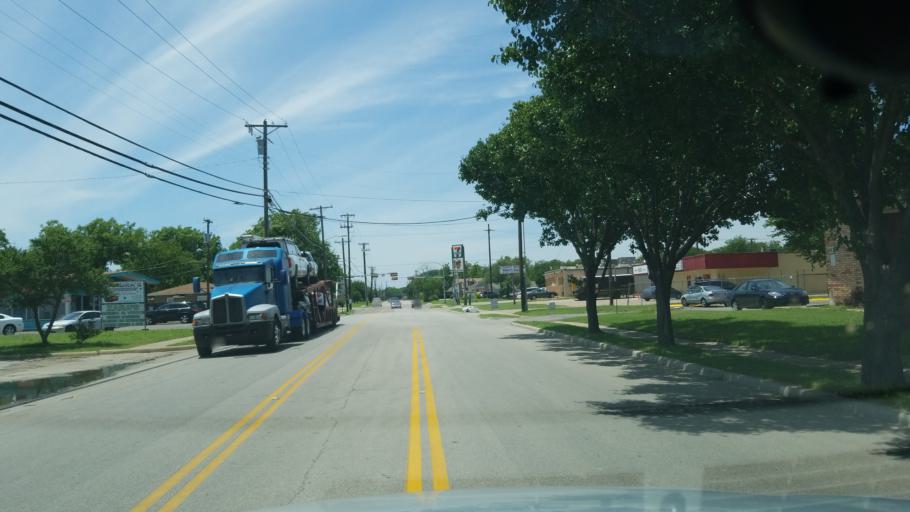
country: US
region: Texas
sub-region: Dallas County
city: Irving
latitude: 32.8176
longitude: -96.9327
